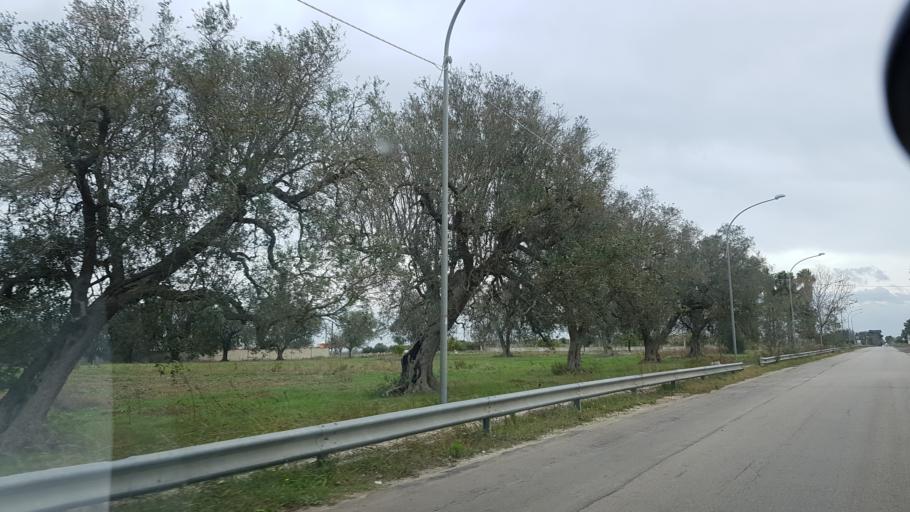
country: IT
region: Apulia
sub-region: Provincia di Brindisi
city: San Pancrazio Salentino
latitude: 40.4161
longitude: 17.8475
